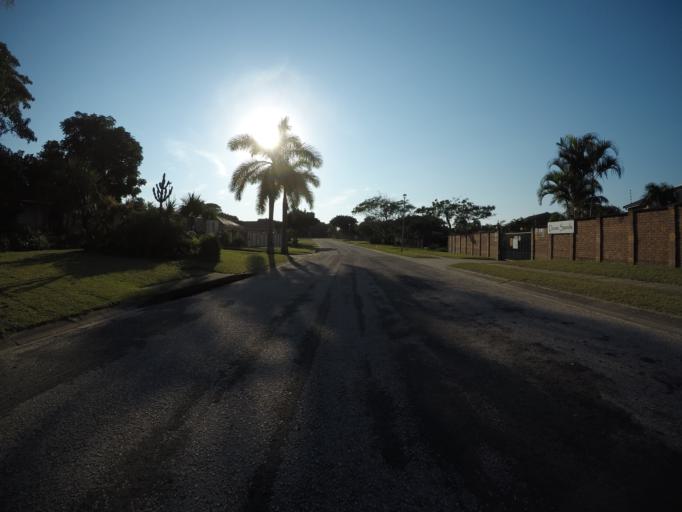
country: ZA
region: KwaZulu-Natal
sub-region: uThungulu District Municipality
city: Richards Bay
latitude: -28.7787
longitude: 32.1039
